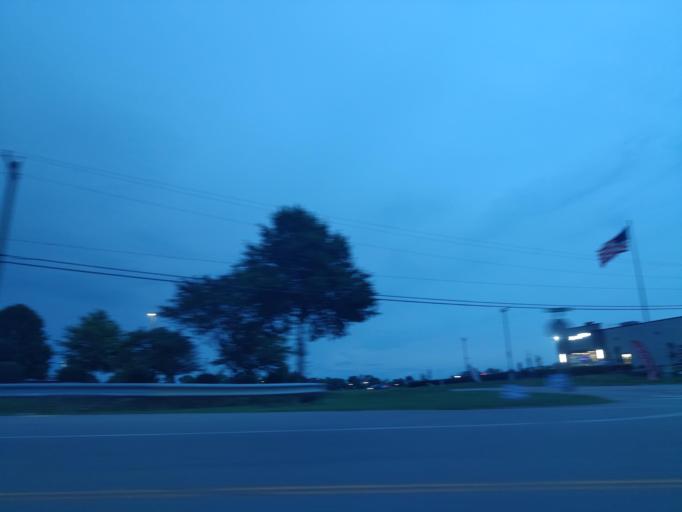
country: US
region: Kentucky
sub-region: Scott County
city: Georgetown
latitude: 38.2306
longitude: -84.5343
